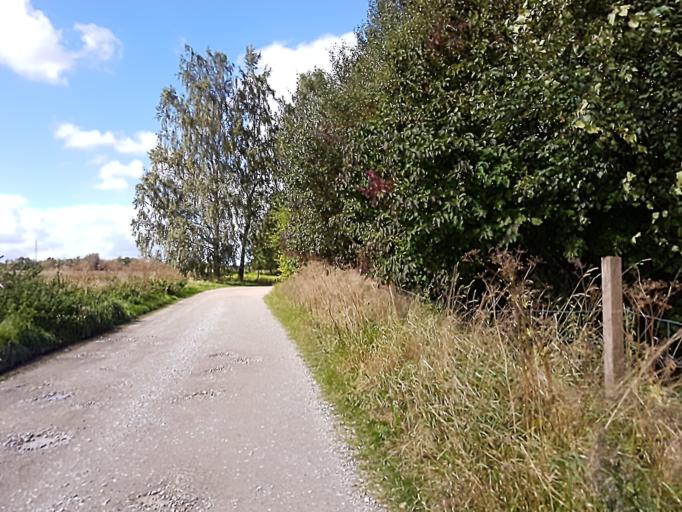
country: DK
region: Capital Region
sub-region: Egedal Kommune
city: Olstykke
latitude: 55.7887
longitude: 12.1333
